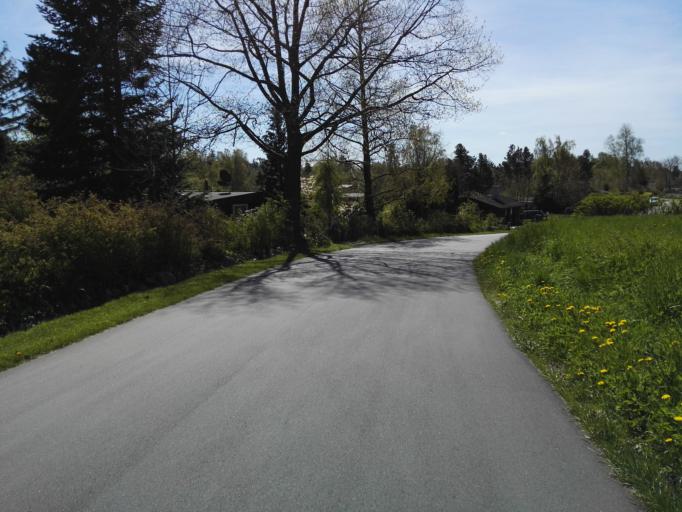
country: DK
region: Capital Region
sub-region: Frederikssund Kommune
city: Frederikssund
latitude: 55.9005
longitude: 12.0544
